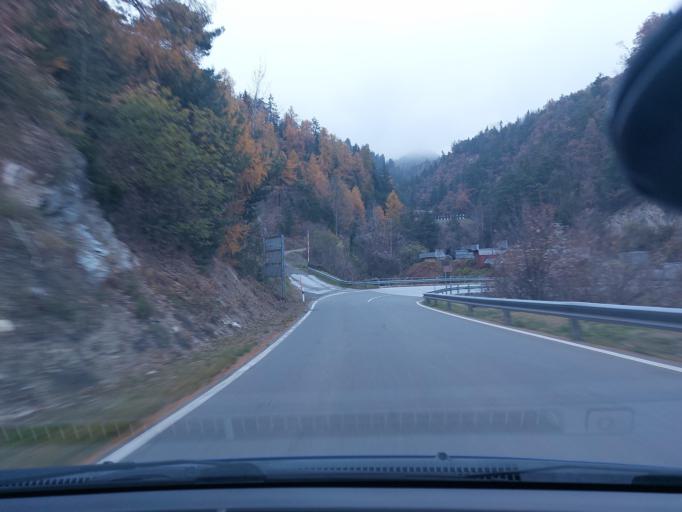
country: CH
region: Valais
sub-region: Sion District
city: Grimisuat
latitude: 46.2637
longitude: 7.3706
